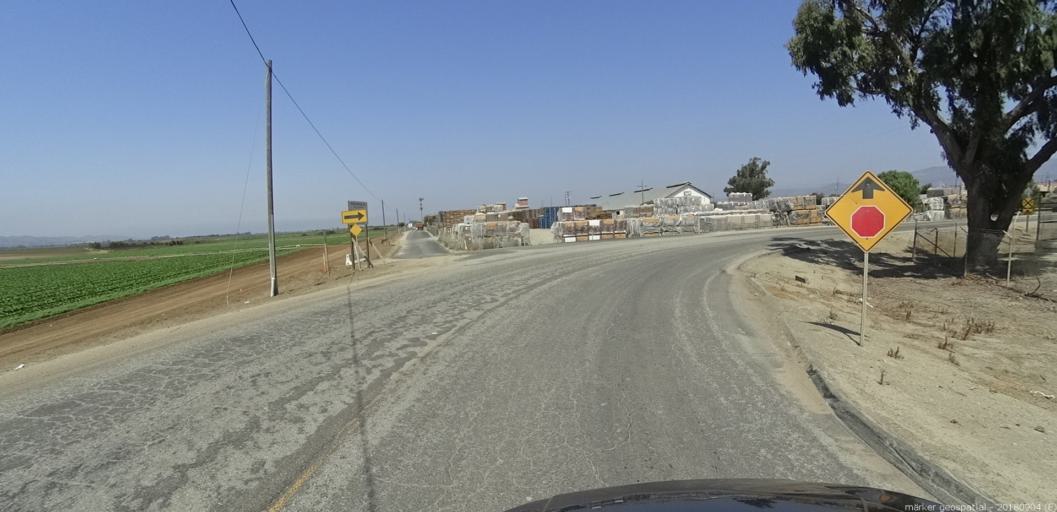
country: US
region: California
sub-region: Monterey County
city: Chualar
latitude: 36.5683
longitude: -121.5189
